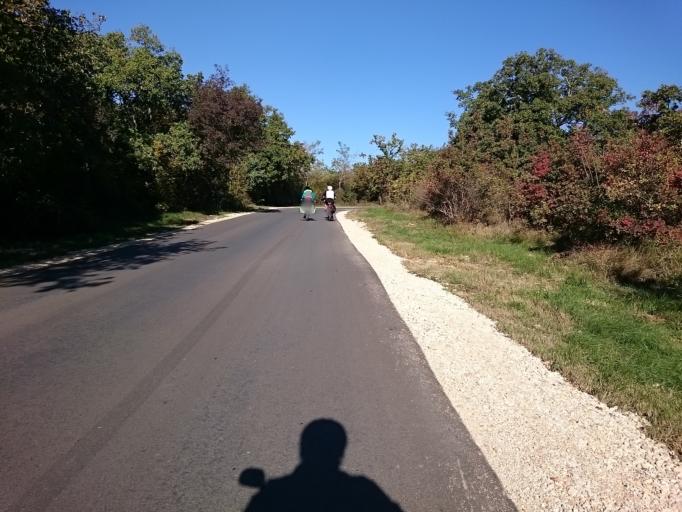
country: HR
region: Istarska
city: Umag
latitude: 45.4559
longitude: 13.5381
